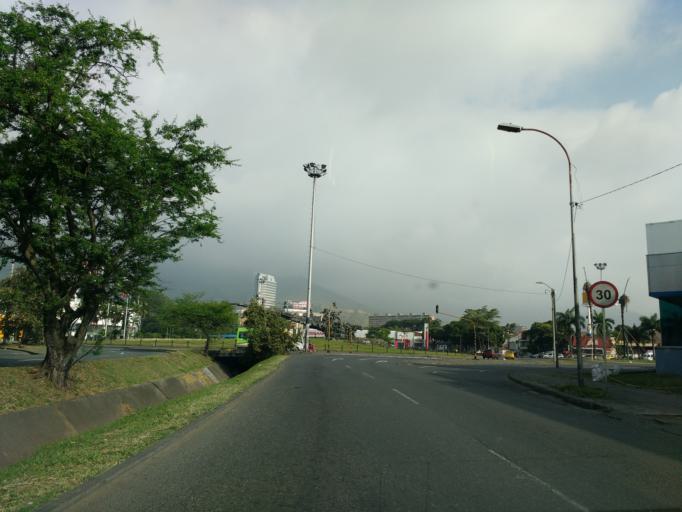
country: CO
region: Valle del Cauca
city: Cali
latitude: 3.4708
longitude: -76.5206
